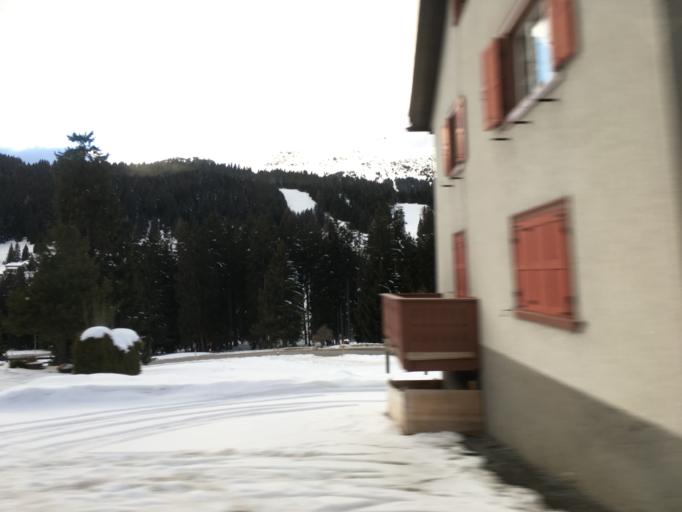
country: CH
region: Grisons
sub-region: Plessur District
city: Churwalden
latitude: 46.7211
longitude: 9.5585
